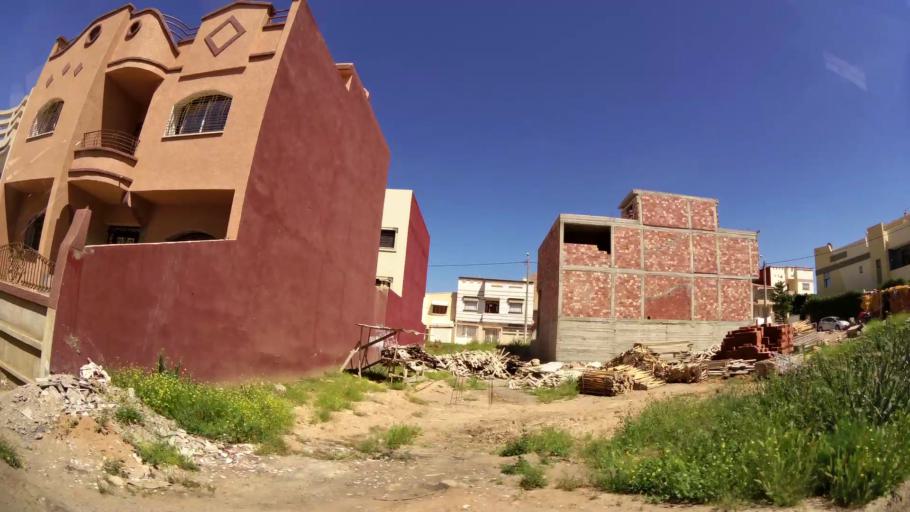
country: MA
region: Oriental
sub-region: Oujda-Angad
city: Oujda
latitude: 34.6474
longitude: -1.9044
